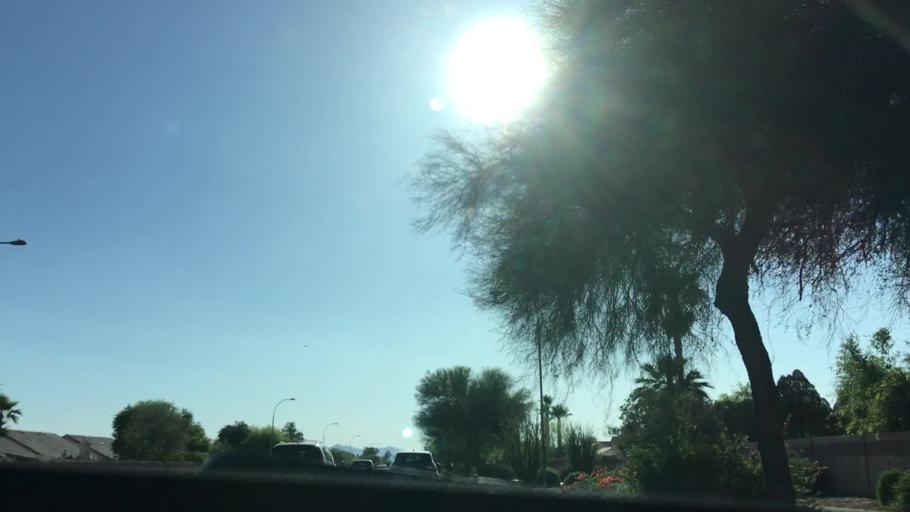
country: US
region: Arizona
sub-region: Maricopa County
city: Peoria
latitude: 33.6109
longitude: -112.2257
